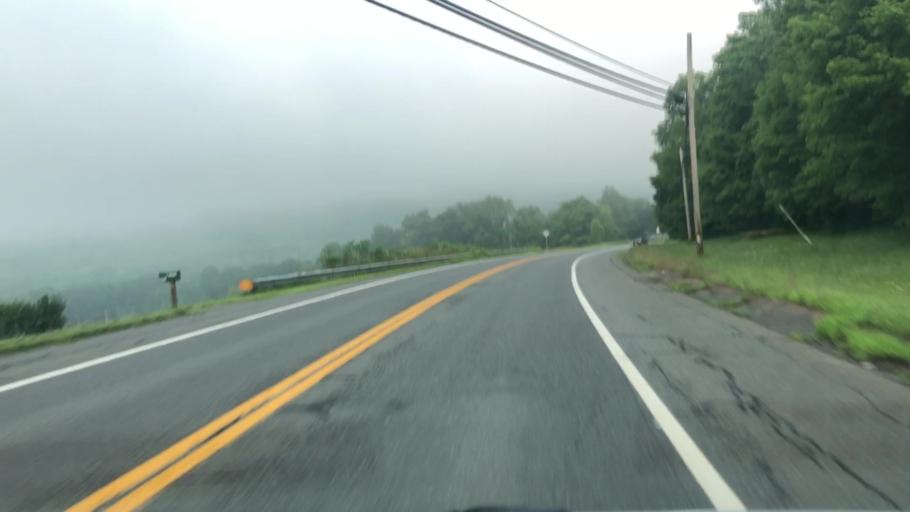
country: US
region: Massachusetts
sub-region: Franklin County
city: Shelburne
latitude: 42.5835
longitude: -72.7065
